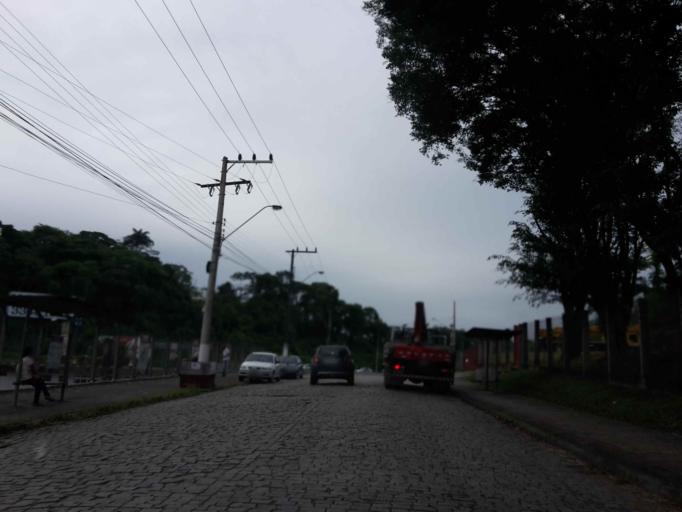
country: BR
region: Santa Catarina
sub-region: Blumenau
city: Blumenau
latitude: -26.8640
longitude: -49.0995
